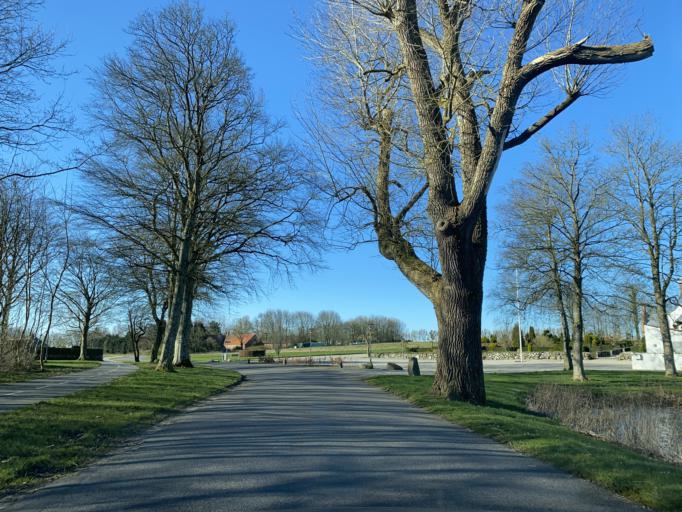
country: DK
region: Central Jutland
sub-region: Skanderborg Kommune
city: Skovby
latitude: 56.1943
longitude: 9.9655
